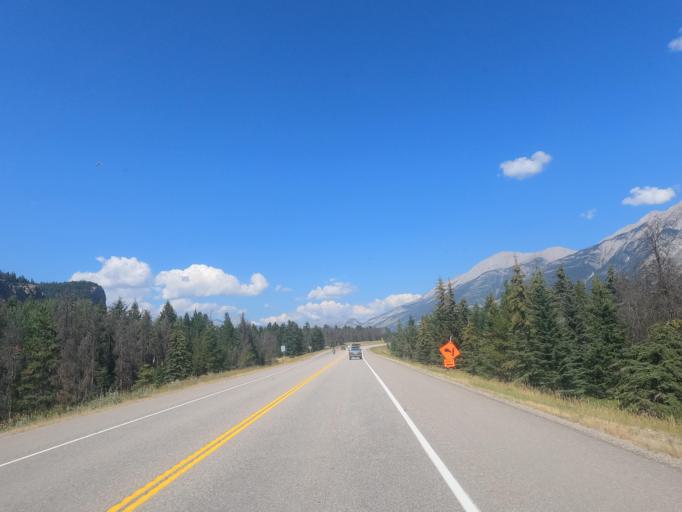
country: CA
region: Alberta
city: Jasper Park Lodge
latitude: 52.9369
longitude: -118.0389
